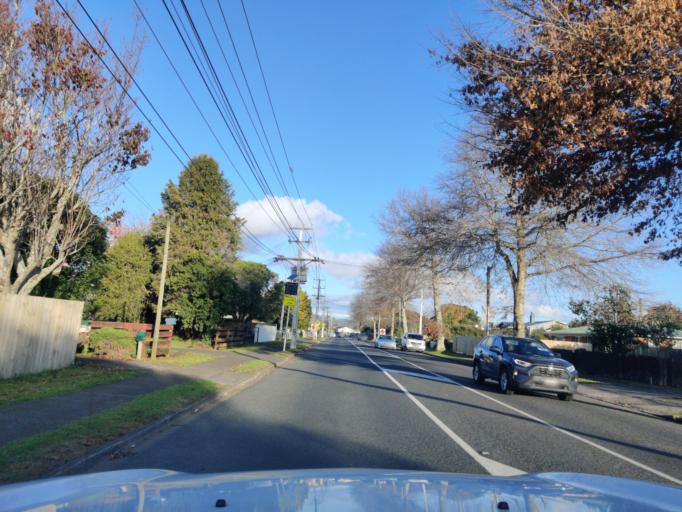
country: NZ
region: Auckland
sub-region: Auckland
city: Red Hill
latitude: -37.0527
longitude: 174.9574
